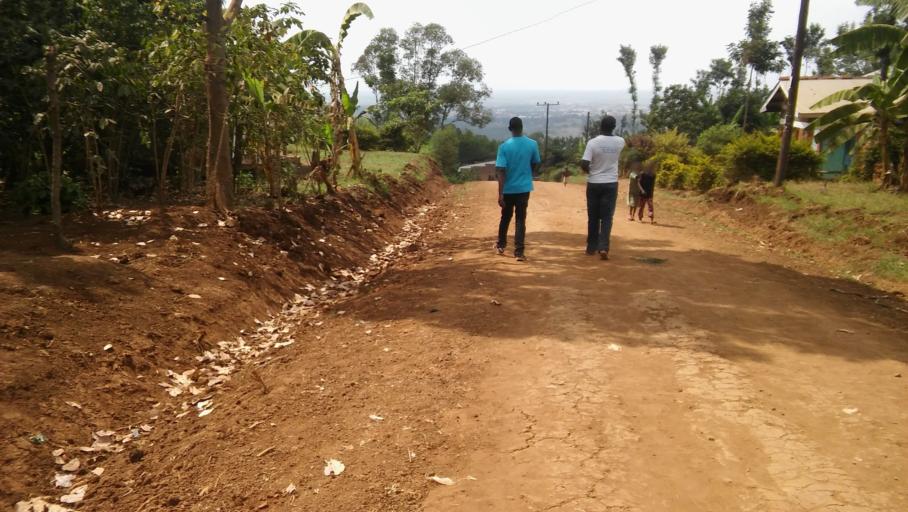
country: UG
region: Eastern Region
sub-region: Mbale District
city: Mbale
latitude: 1.0579
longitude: 34.2130
